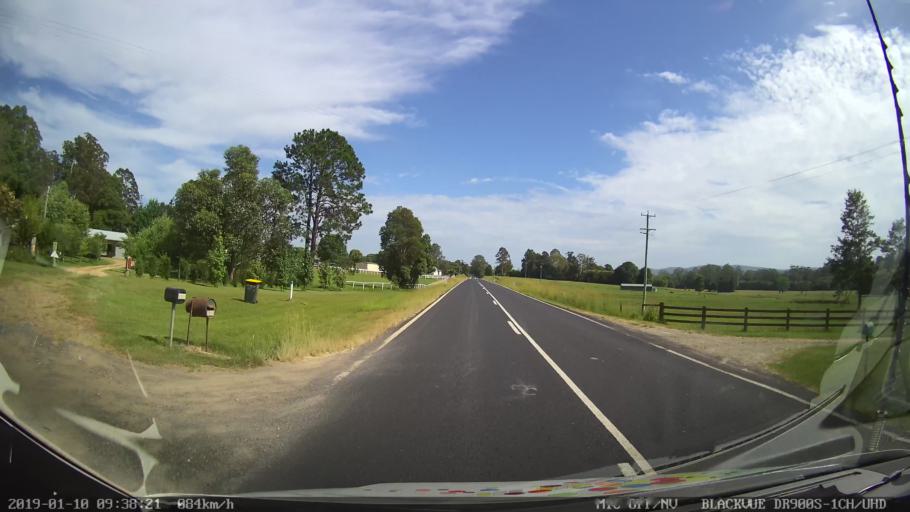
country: AU
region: New South Wales
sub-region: Coffs Harbour
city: Nana Glen
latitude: -30.1772
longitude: 153.0076
